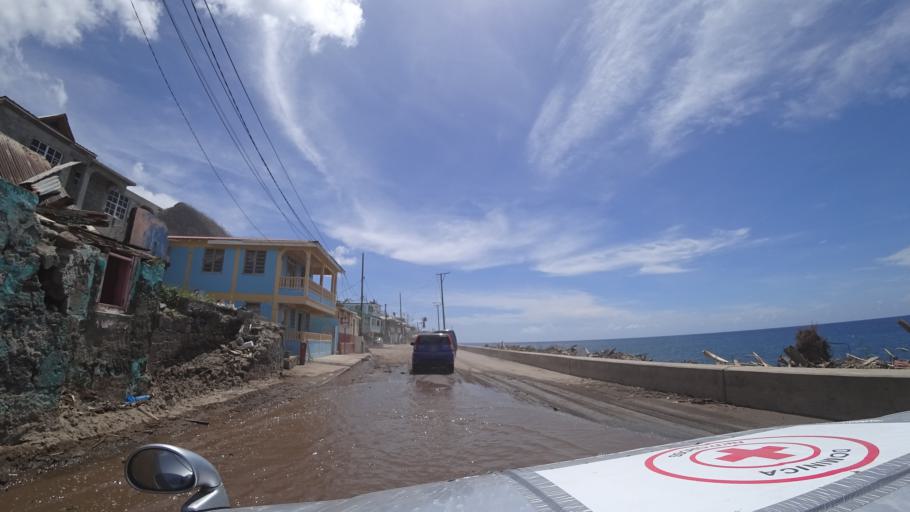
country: DM
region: Saint Luke
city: Pointe Michel
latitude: 15.2631
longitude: -61.3773
